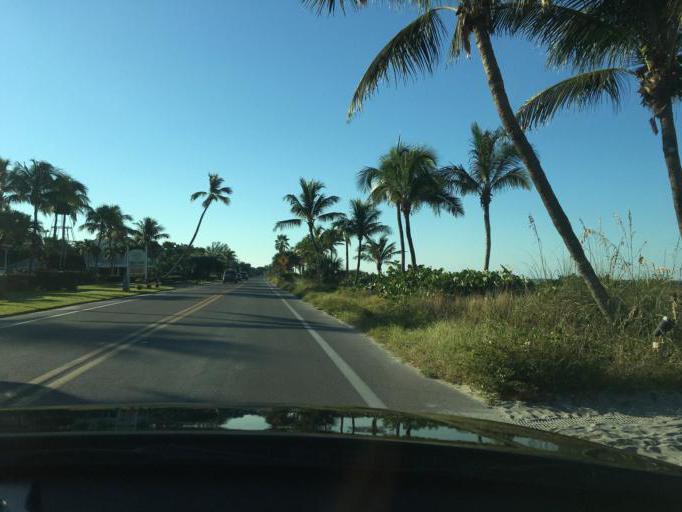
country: US
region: Florida
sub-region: Lee County
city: Saint James City
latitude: 26.5109
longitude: -82.1907
